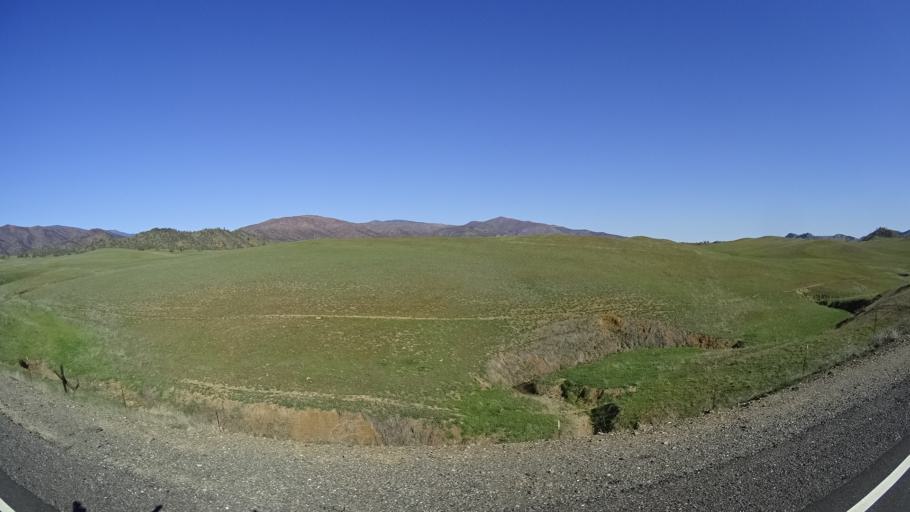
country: US
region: California
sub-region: Glenn County
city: Orland
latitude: 39.6591
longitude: -122.5503
